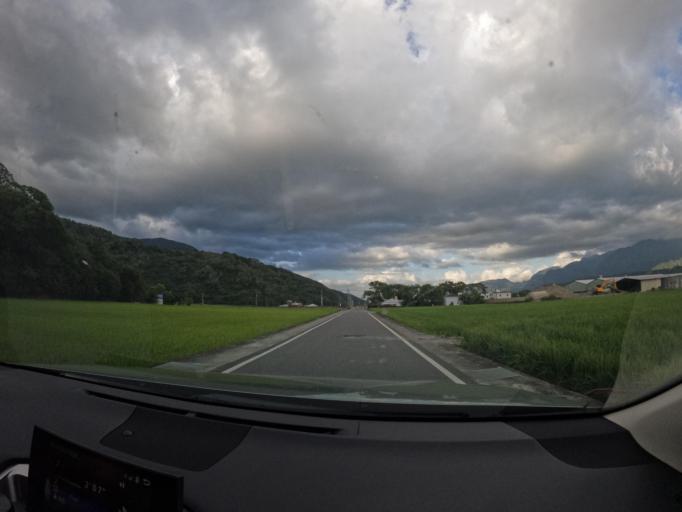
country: TW
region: Taiwan
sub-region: Taitung
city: Taitung
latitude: 23.1526
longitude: 121.2236
